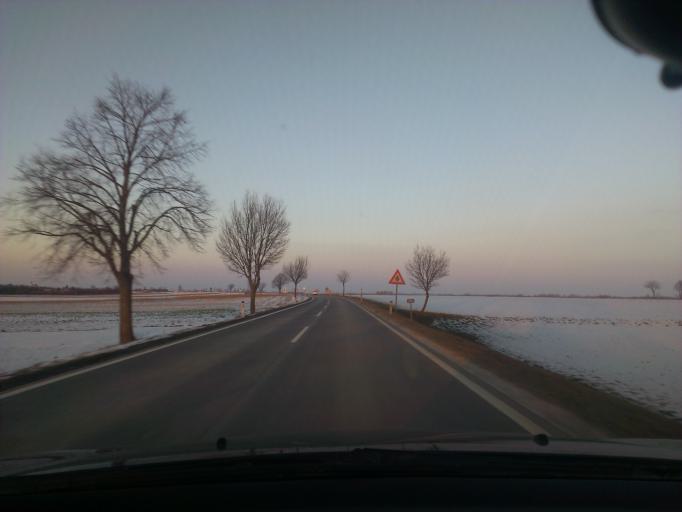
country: AT
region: Lower Austria
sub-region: Politischer Bezirk Baden
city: Seibersdorf
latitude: 47.9803
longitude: 16.5112
